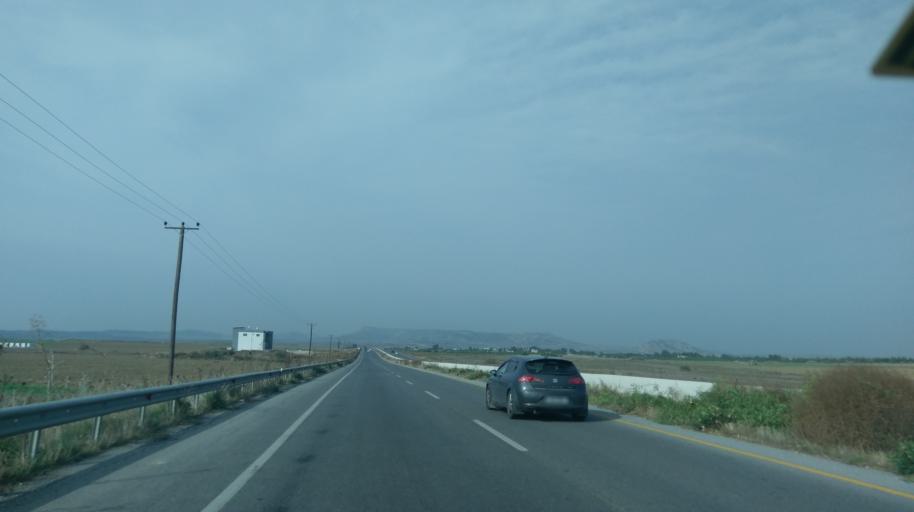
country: CY
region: Lefkosia
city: Mammari
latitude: 35.2123
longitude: 33.2021
